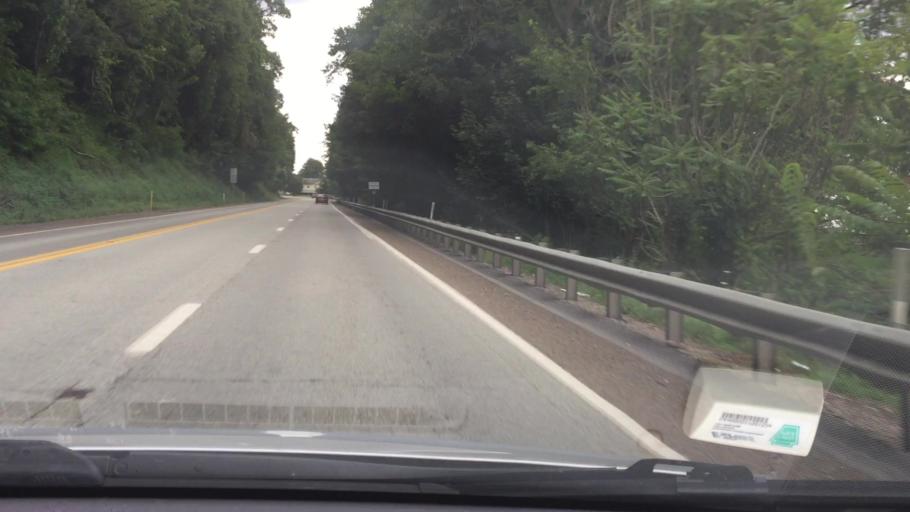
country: US
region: Pennsylvania
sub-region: Armstrong County
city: Freeport
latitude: 40.6782
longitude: -79.6926
